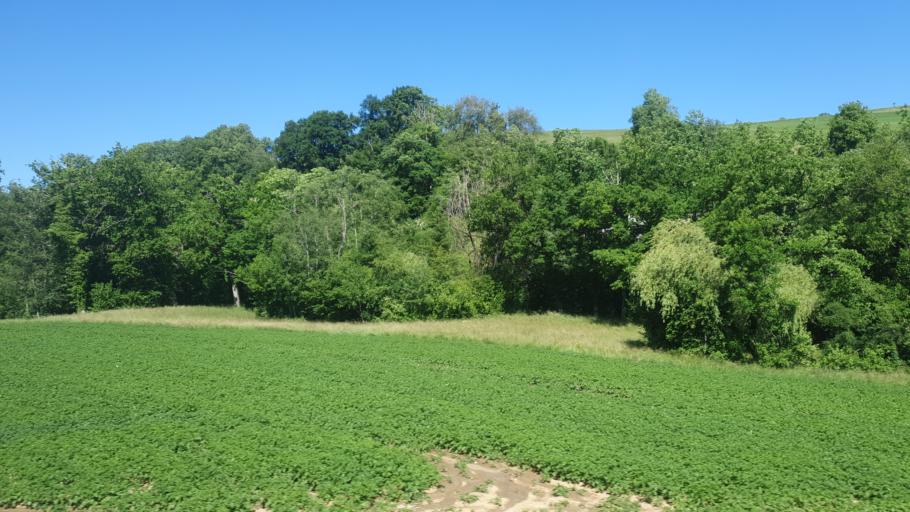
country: CH
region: Fribourg
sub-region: Sarine District
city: Givisiez
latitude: 46.8363
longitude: 7.1278
